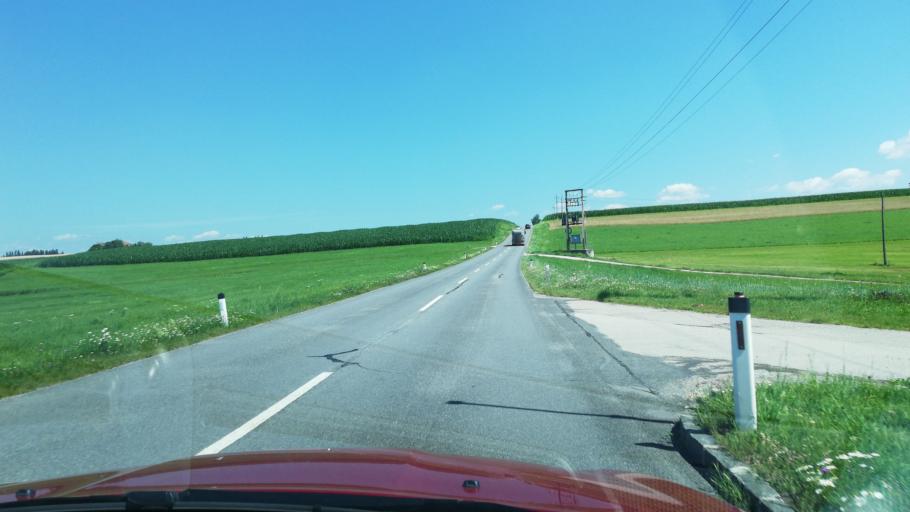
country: AT
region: Upper Austria
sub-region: Politischer Bezirk Urfahr-Umgebung
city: Herzogsdorf
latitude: 48.4482
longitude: 14.0554
